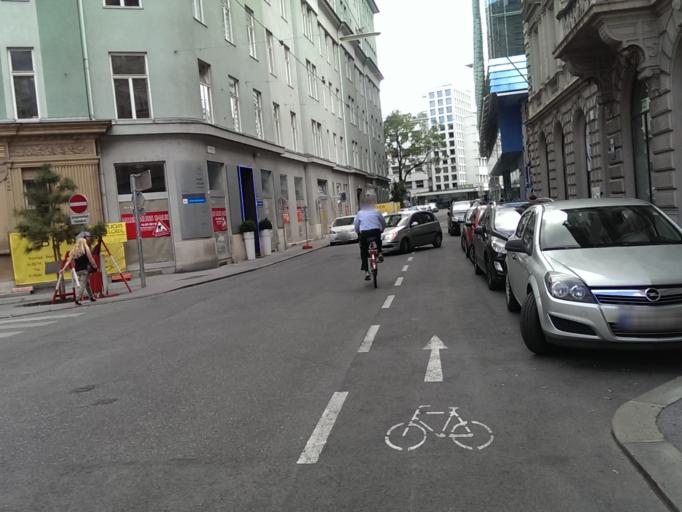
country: AT
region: Styria
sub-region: Graz Stadt
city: Graz
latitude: 47.0696
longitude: 15.4382
